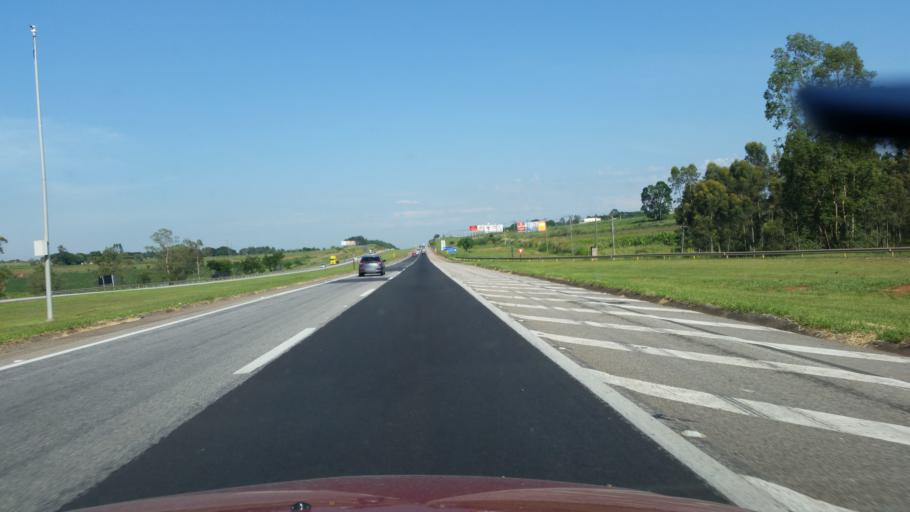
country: BR
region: Sao Paulo
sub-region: Porto Feliz
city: Porto Feliz
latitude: -23.3431
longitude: -47.5312
